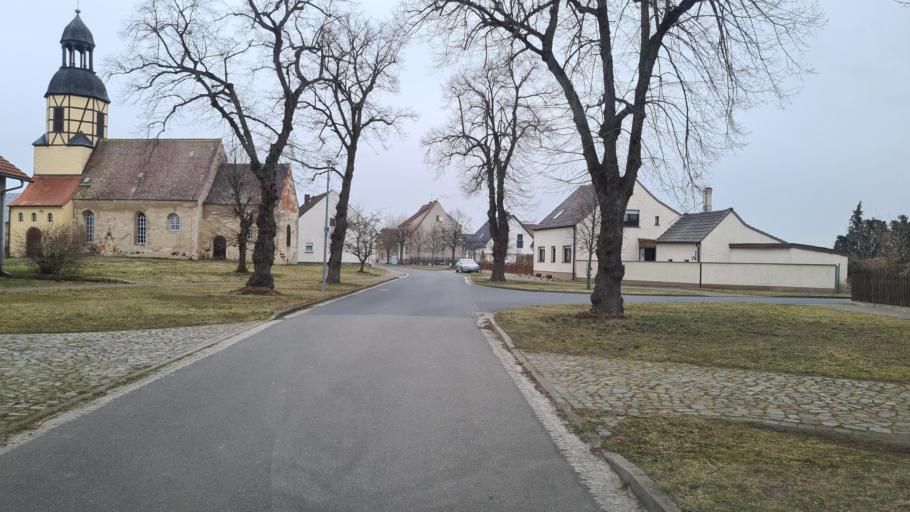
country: DE
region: Brandenburg
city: Herzberg
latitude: 51.6464
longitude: 13.1904
